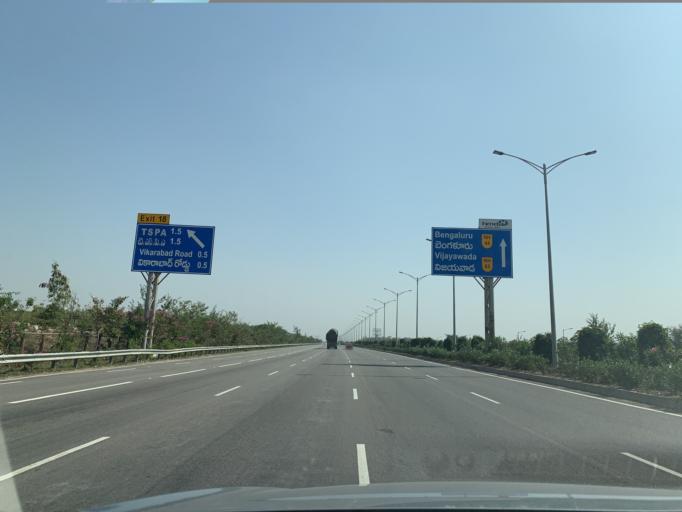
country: IN
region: Telangana
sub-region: Hyderabad
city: Hyderabad
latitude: 17.3602
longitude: 78.3544
